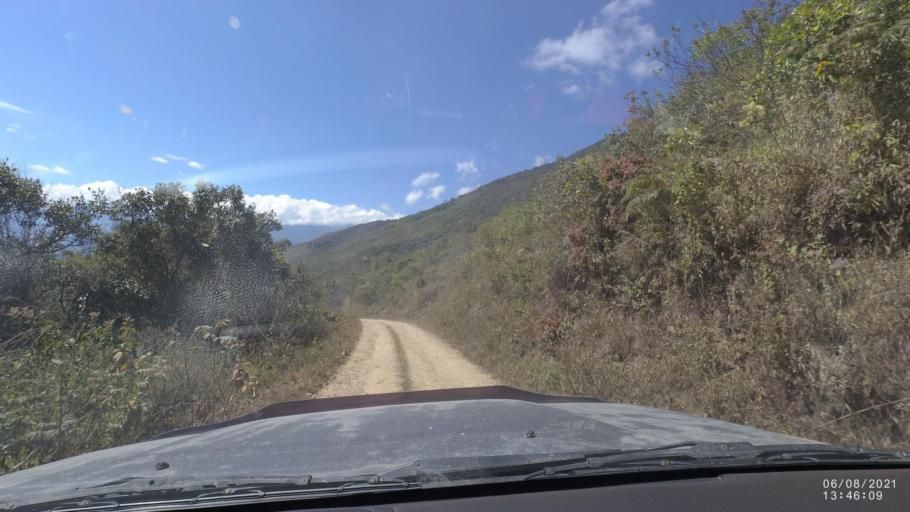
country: BO
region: La Paz
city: Quime
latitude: -16.6700
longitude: -66.7291
